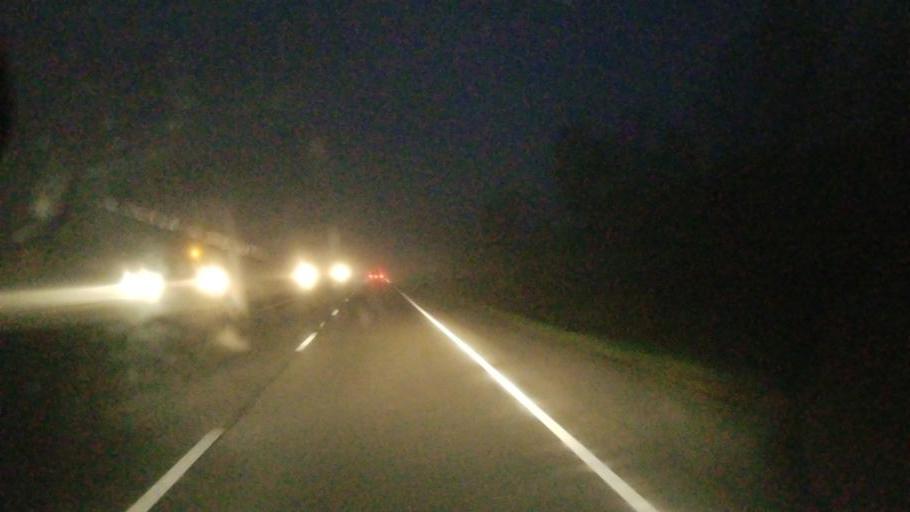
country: US
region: Ohio
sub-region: Ross County
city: Kingston
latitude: 39.4534
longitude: -82.9718
